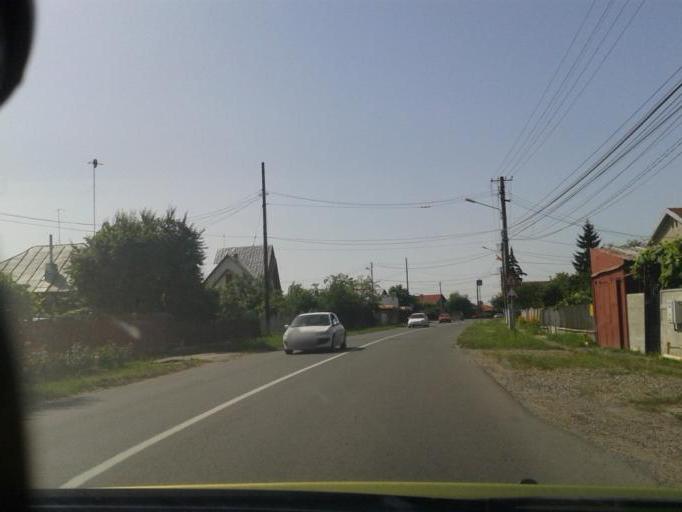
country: RO
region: Prahova
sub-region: Comuna Paulesti
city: Gageni
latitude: 45.0301
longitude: 25.9434
